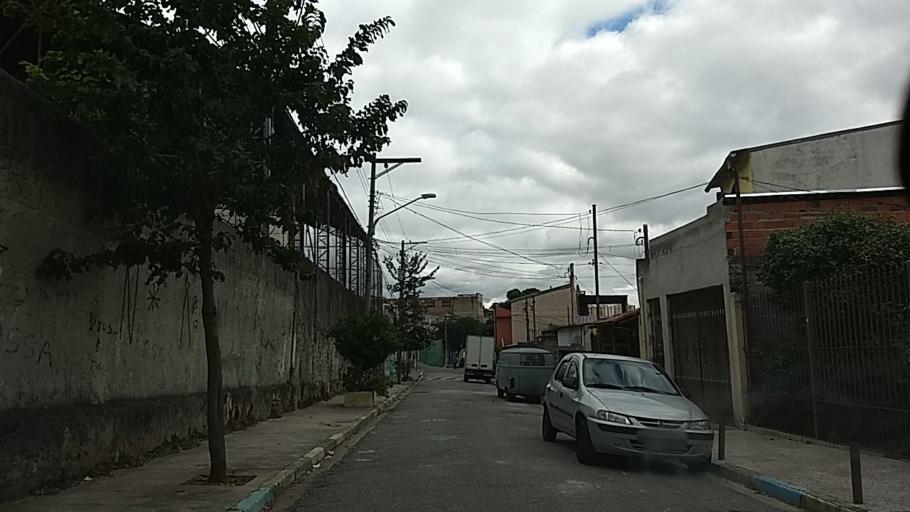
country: BR
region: Sao Paulo
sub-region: Guarulhos
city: Guarulhos
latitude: -23.4919
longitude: -46.5865
